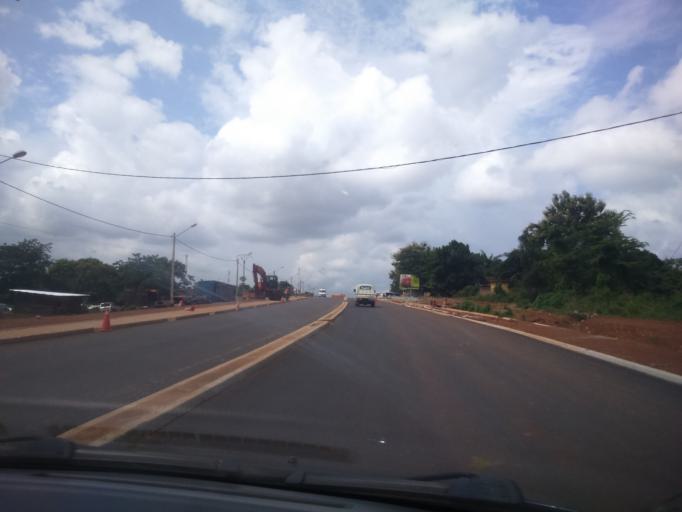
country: CI
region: Moyen-Comoe
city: Abengourou
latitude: 6.7186
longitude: -3.5178
